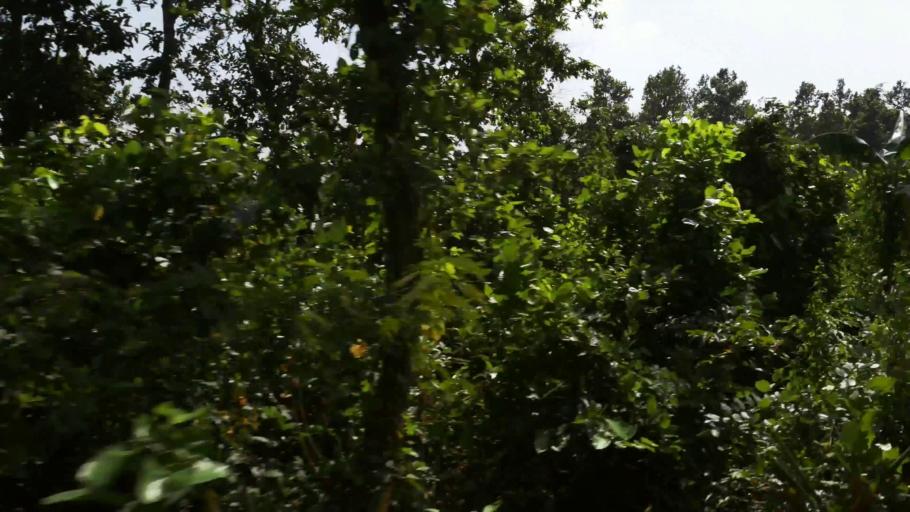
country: BD
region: Dhaka
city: Tungi
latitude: 24.1395
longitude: 90.4617
